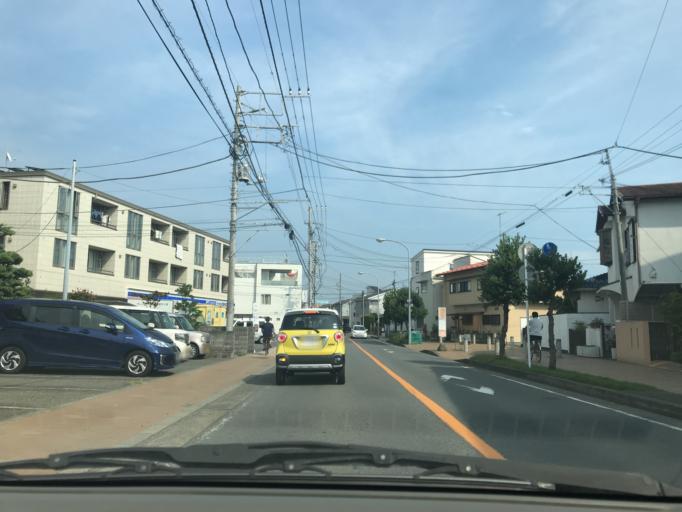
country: JP
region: Kanagawa
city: Chigasaki
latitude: 35.3243
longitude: 139.4024
